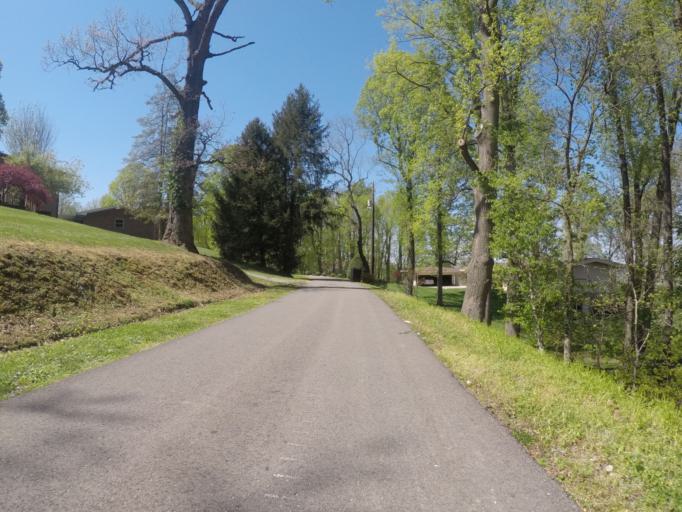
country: US
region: West Virginia
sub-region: Wayne County
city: Kenova
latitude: 38.3939
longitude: -82.5790
